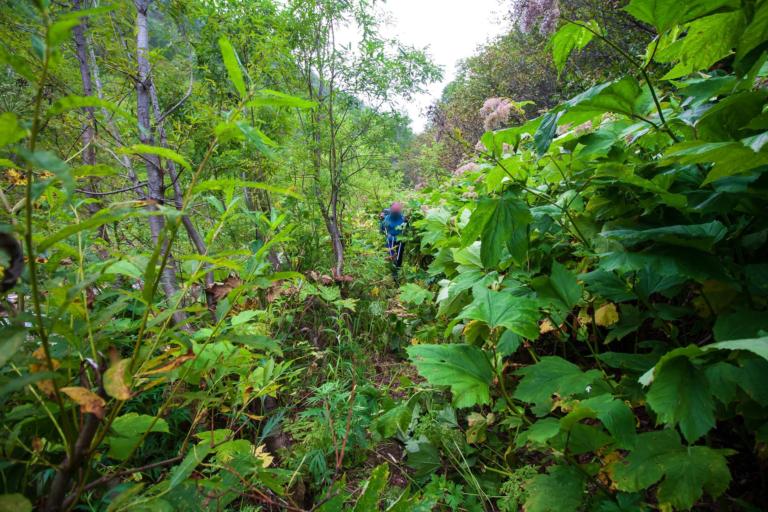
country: RU
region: Kamtsjatka
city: Yelizovo
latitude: 54.0447
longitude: 158.0504
